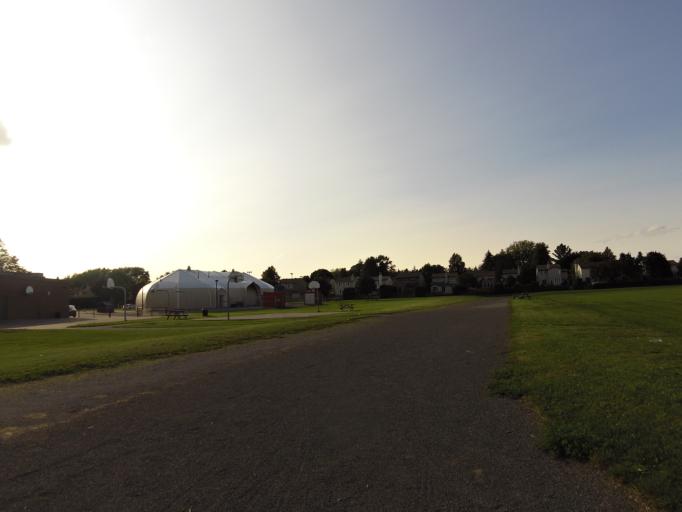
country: CA
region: Ontario
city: Ottawa
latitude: 45.3505
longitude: -75.7158
